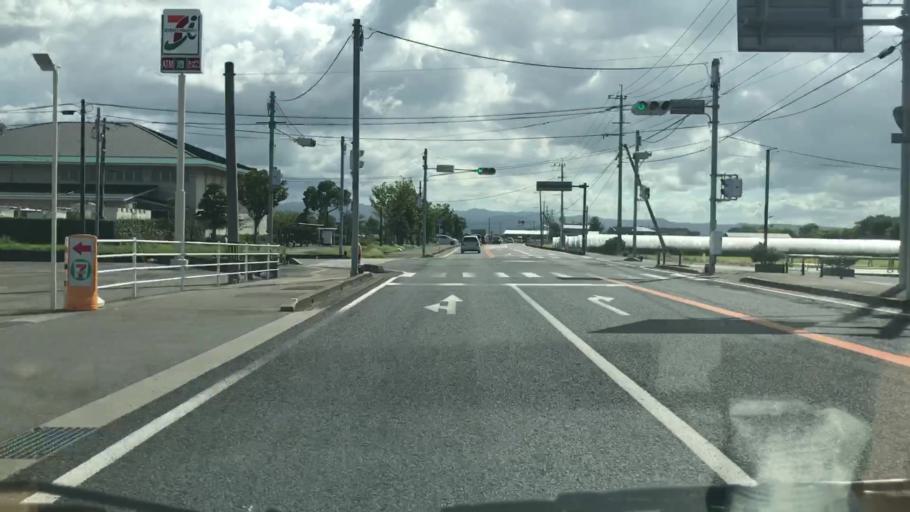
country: JP
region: Saga Prefecture
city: Kashima
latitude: 33.1817
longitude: 130.1897
